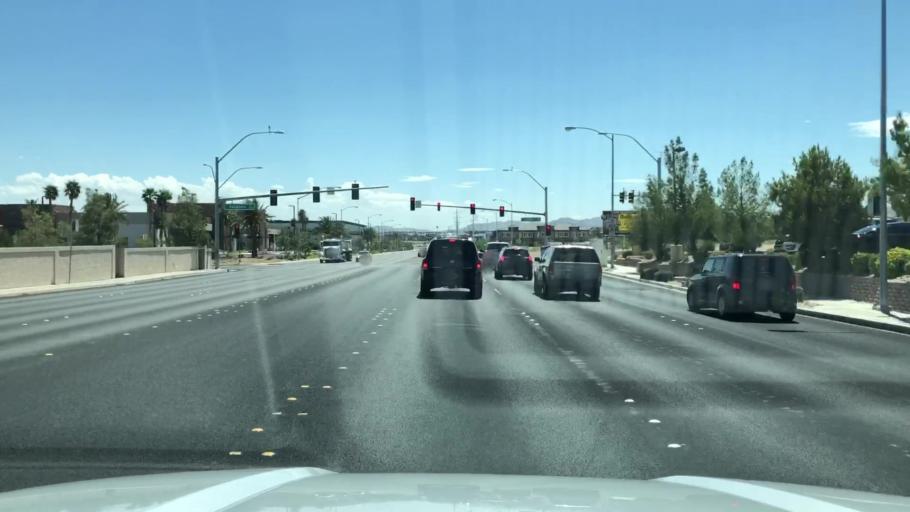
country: US
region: Nevada
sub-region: Clark County
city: Spring Valley
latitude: 36.0935
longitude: -115.2794
